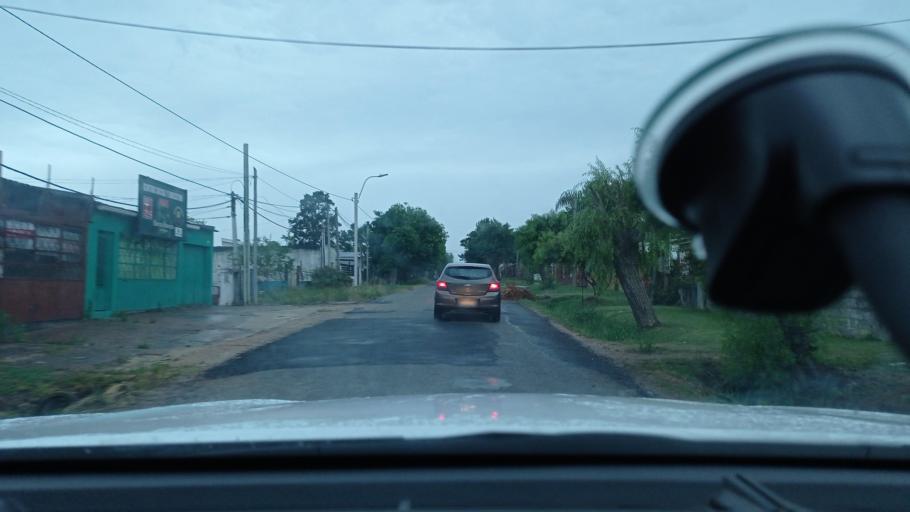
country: UY
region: Canelones
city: Joaquin Suarez
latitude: -34.7544
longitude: -56.0142
